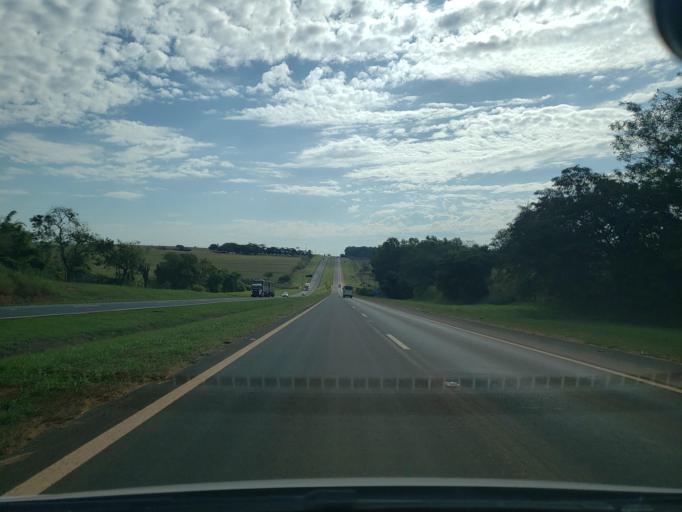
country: BR
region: Sao Paulo
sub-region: Promissao
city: Promissao
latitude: -21.6118
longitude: -49.8676
